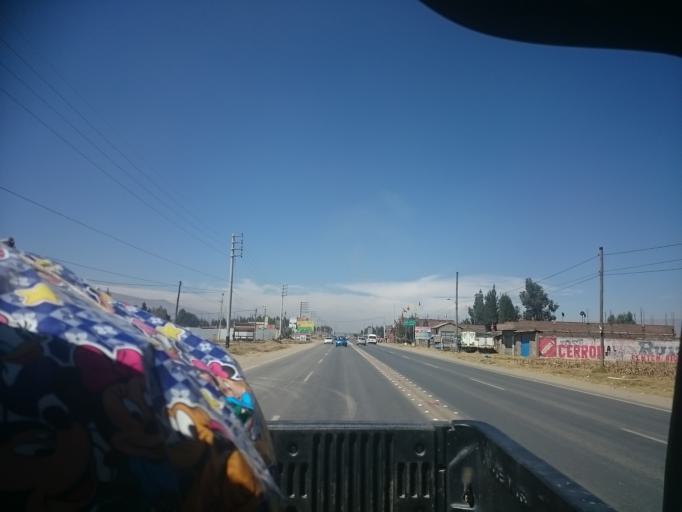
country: PE
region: Junin
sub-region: Provincia de Huancayo
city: San Jeronimo
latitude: -11.9642
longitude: -75.2724
